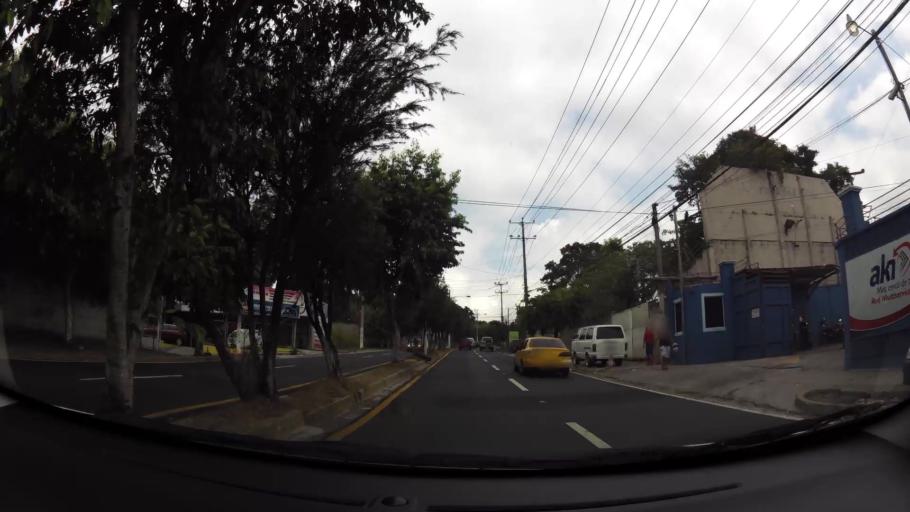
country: SV
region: San Salvador
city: Mejicanos
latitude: 13.7144
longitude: -89.2309
